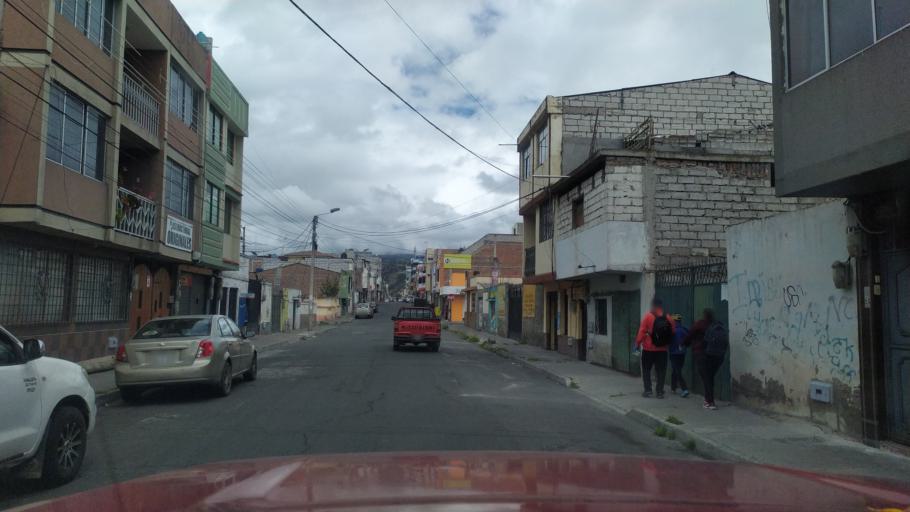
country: EC
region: Chimborazo
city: Riobamba
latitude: -1.6692
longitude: -78.6430
